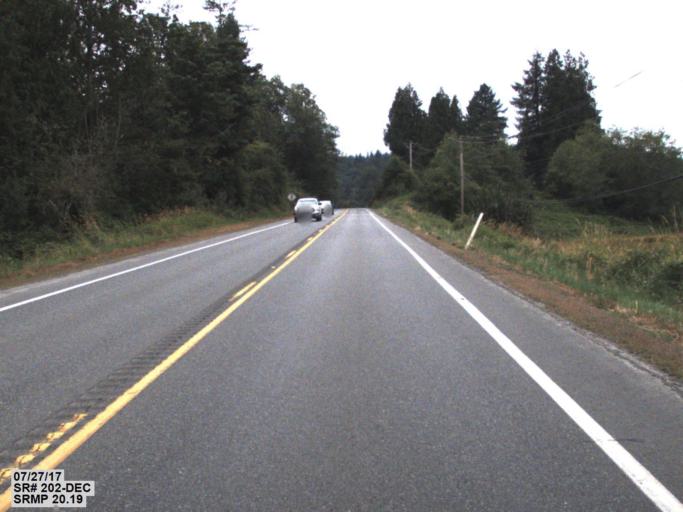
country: US
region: Washington
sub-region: King County
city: Fall City
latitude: 47.5749
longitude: -121.9174
